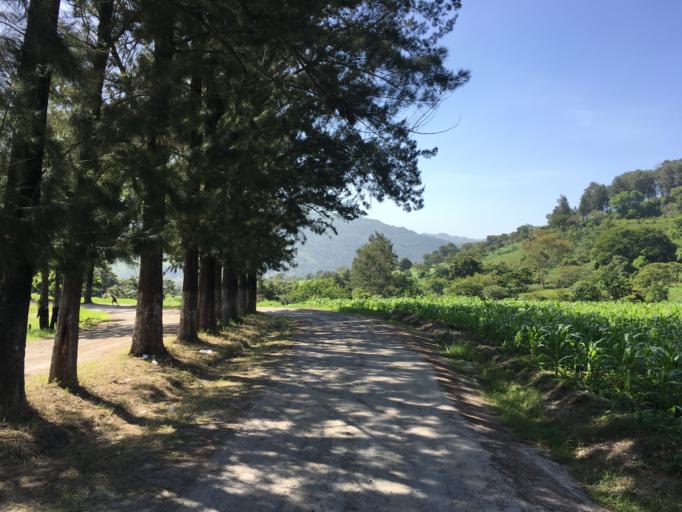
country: GT
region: Guatemala
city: Villa Canales
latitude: 14.4837
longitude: -90.5452
